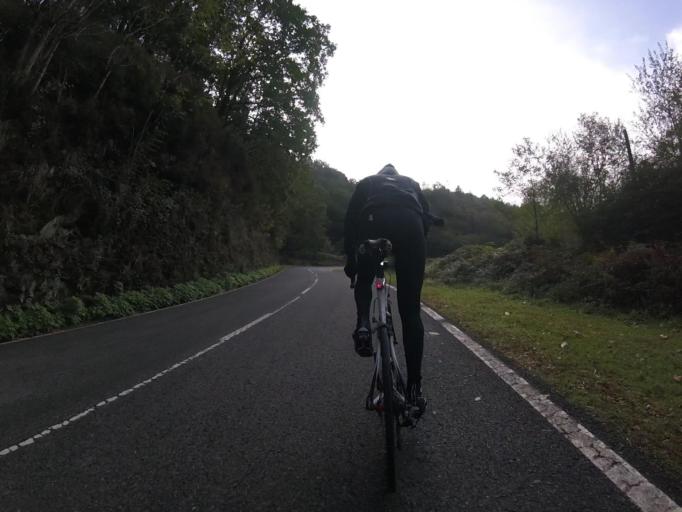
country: ES
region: Navarre
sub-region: Provincia de Navarra
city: Arano
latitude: 43.2081
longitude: -1.8801
